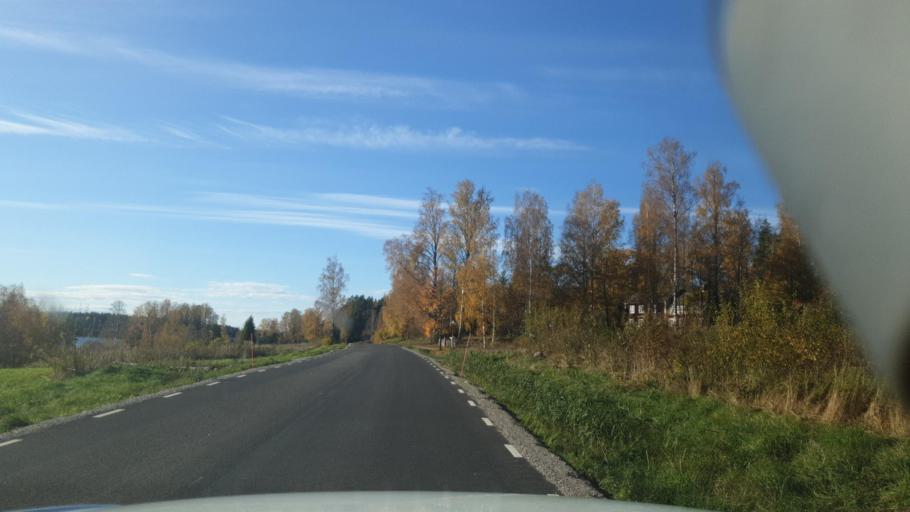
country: SE
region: Vaermland
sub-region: Arvika Kommun
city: Arvika
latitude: 59.6612
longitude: 12.7094
